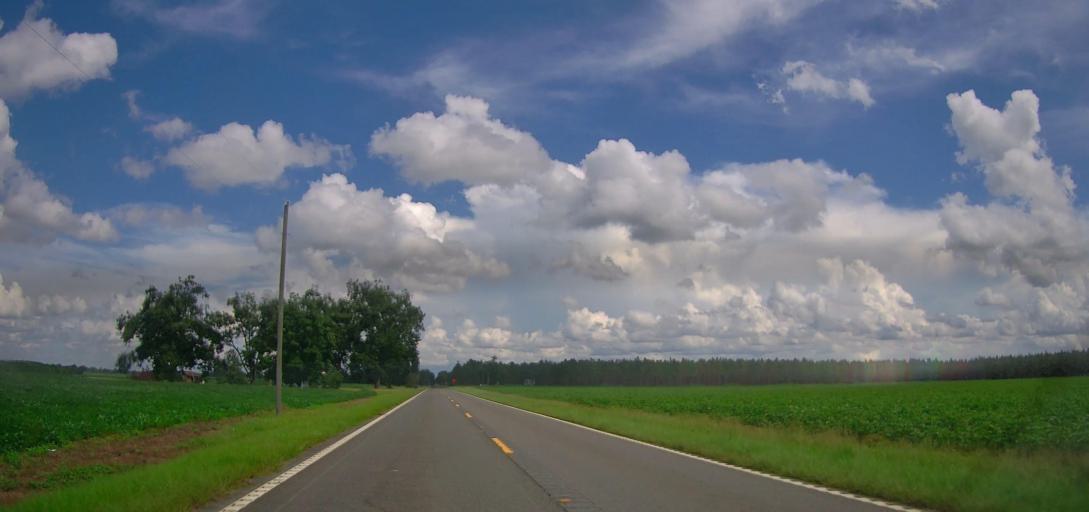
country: US
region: Georgia
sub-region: Taylor County
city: Reynolds
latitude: 32.4403
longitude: -84.1363
